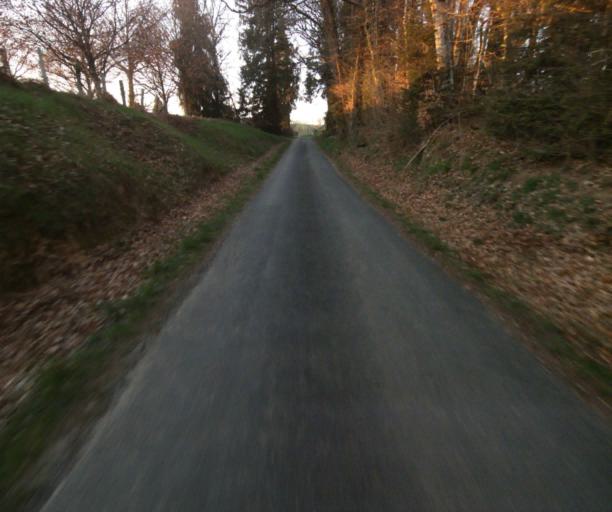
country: FR
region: Limousin
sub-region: Departement de la Correze
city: Uzerche
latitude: 45.3705
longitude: 1.6125
